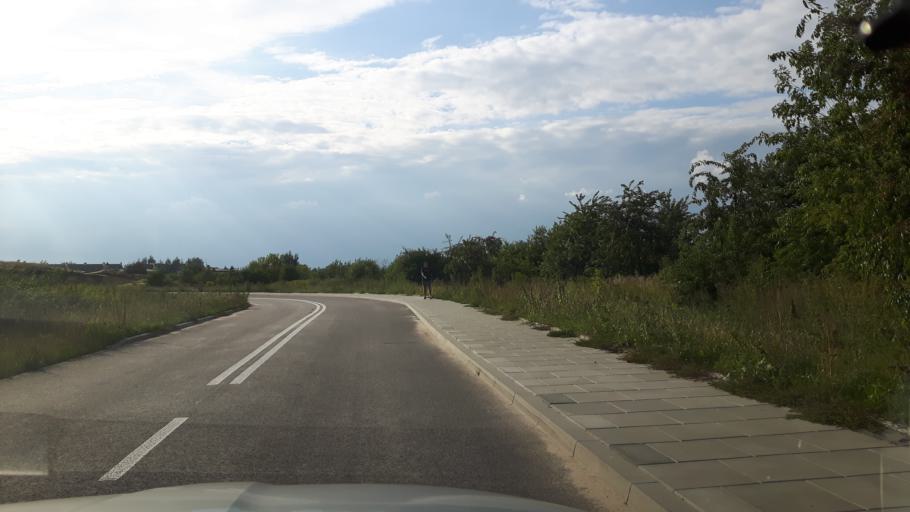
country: PL
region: Masovian Voivodeship
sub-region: Powiat wolominski
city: Marki
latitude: 52.3252
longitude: 21.0846
